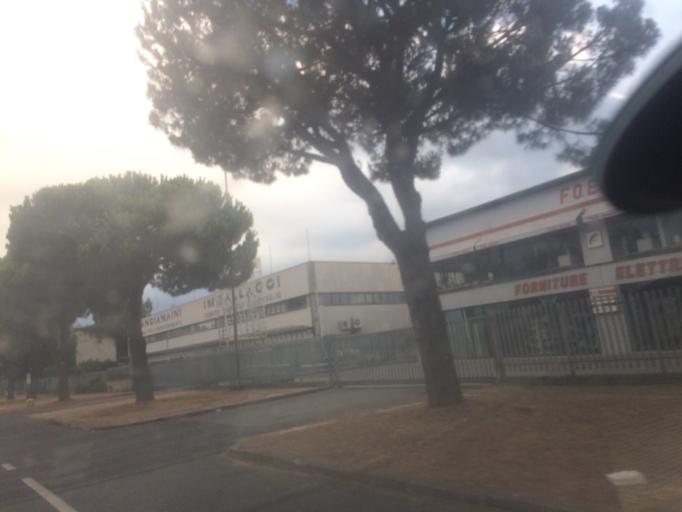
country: IT
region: Tuscany
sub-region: Provincia di Massa-Carrara
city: Massa
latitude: 44.0265
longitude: 10.1087
